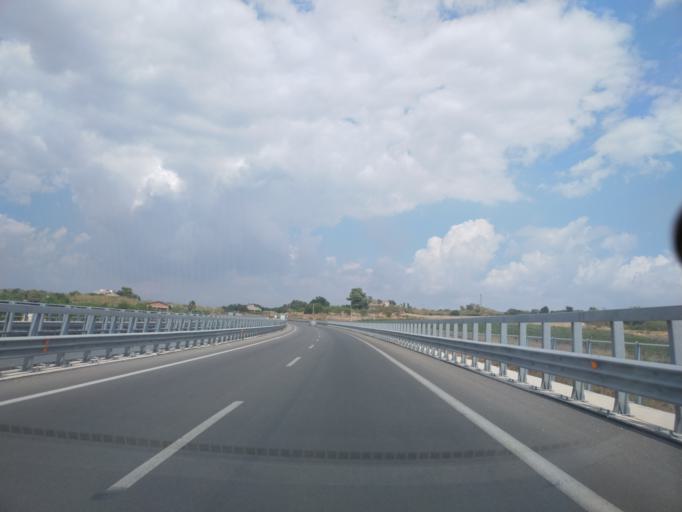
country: IT
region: Sicily
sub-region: Agrigento
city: Grotte
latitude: 37.3623
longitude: 13.7011
